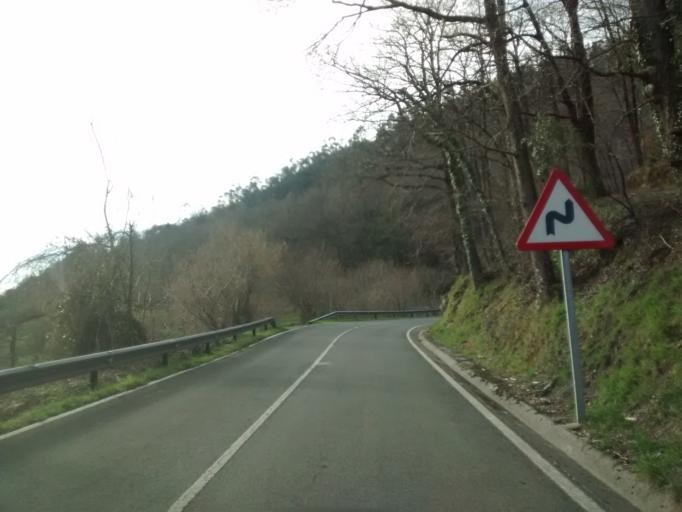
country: ES
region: Cantabria
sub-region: Provincia de Cantabria
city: Arredondo
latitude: 43.2784
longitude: -3.6114
